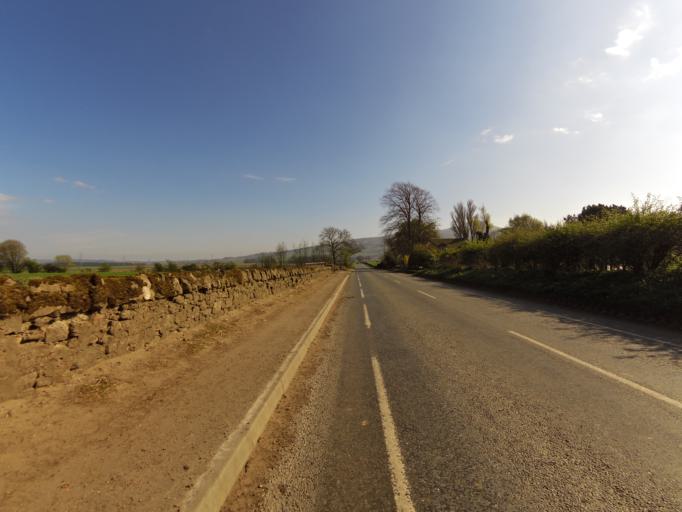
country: GB
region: Scotland
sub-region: Fife
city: Falkland
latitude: 56.2743
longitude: -3.2121
